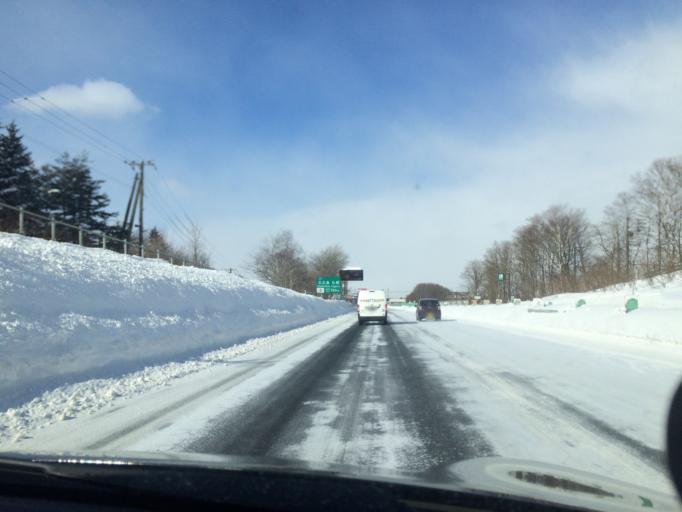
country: JP
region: Hokkaido
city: Kitahiroshima
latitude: 42.9712
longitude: 141.4861
